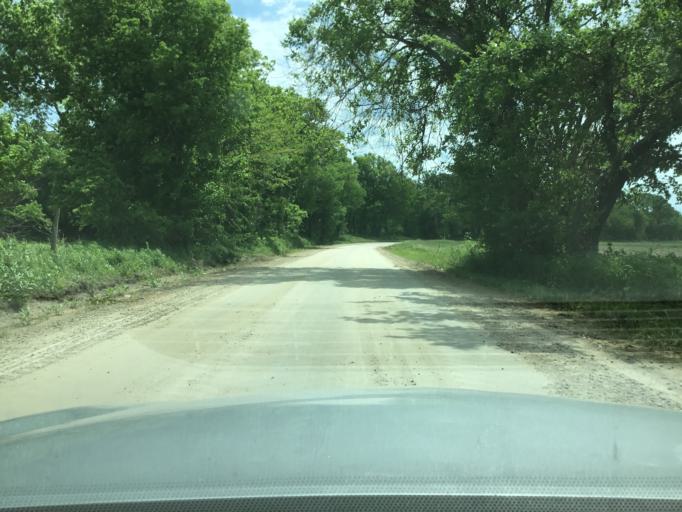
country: US
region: Kansas
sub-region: Montgomery County
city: Coffeyville
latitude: 37.0071
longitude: -95.6066
